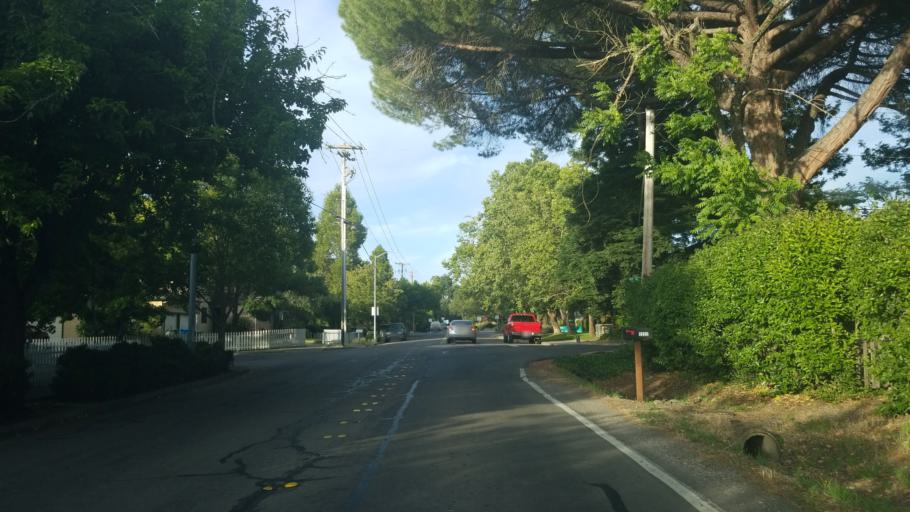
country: US
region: California
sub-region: Sonoma County
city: Santa Rosa
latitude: 38.4517
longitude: -122.7368
